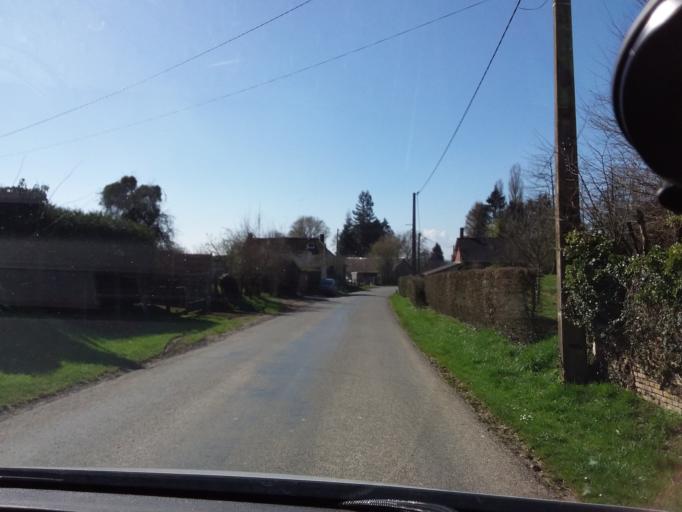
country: FR
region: Picardie
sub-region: Departement de l'Aisne
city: Montcornet
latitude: 49.7492
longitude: 3.9997
